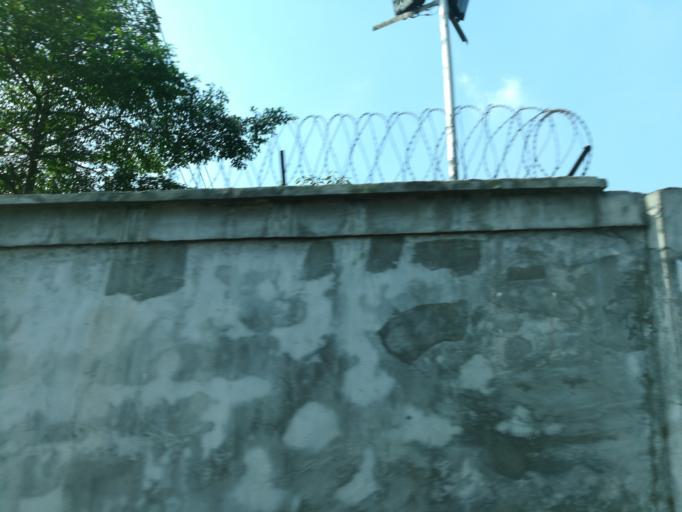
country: NG
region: Rivers
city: Port Harcourt
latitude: 4.8311
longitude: 6.9939
